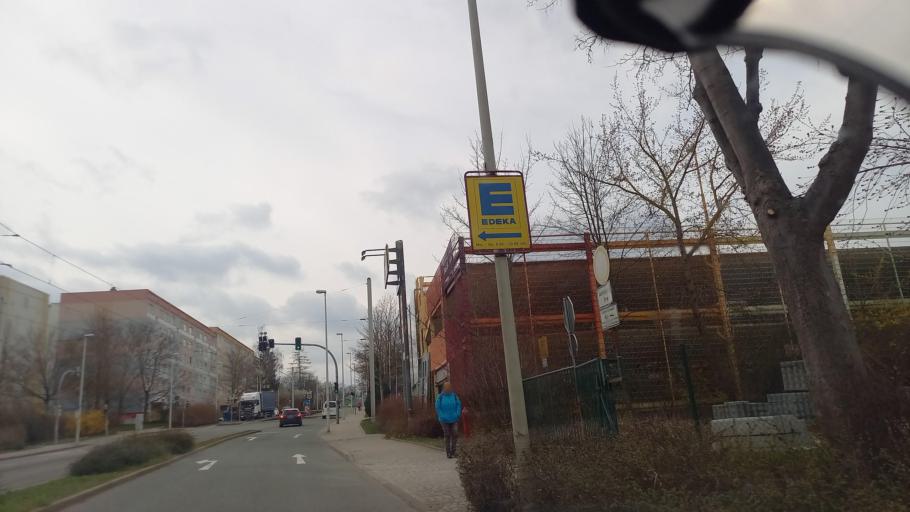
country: DE
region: Saxony
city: Lichtentanne
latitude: 50.6916
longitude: 12.4643
